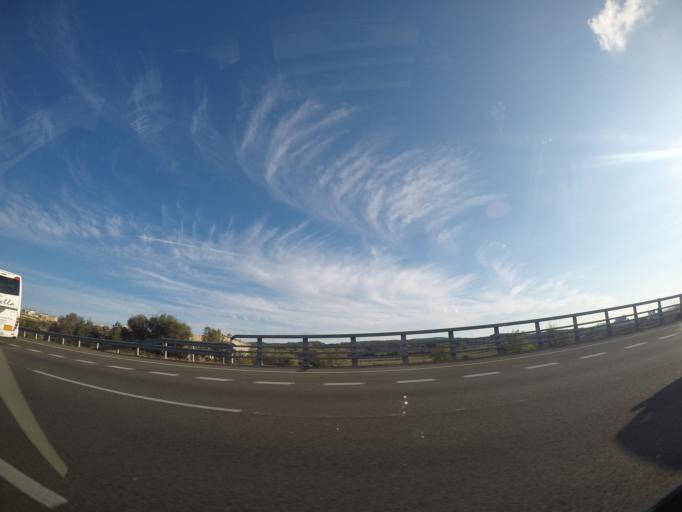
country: ES
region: Catalonia
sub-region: Provincia de Barcelona
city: Vilafranca del Penedes
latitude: 41.3277
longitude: 1.6799
